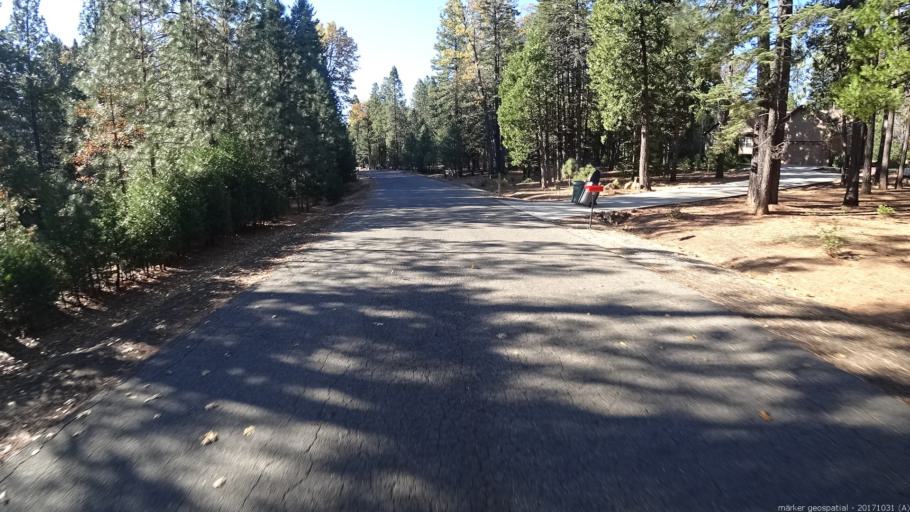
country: US
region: California
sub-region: Shasta County
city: Shingletown
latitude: 40.4954
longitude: -121.8872
